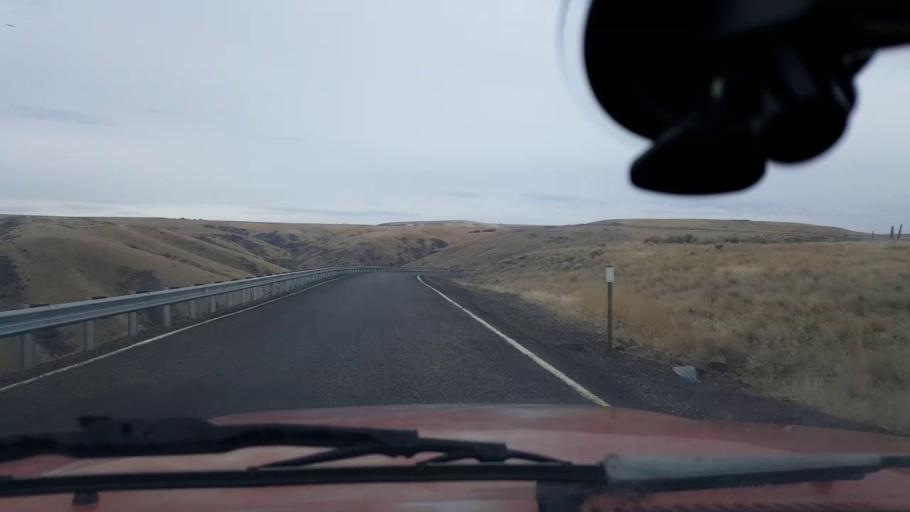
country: US
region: Washington
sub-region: Asotin County
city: Clarkston Heights-Vineland
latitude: 46.3328
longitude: -117.2923
